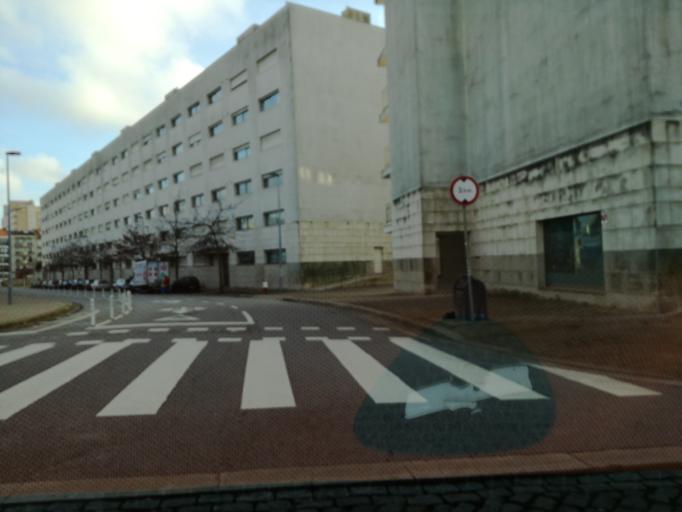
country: PT
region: Porto
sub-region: Porto
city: Porto
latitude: 41.1668
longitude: -8.6318
